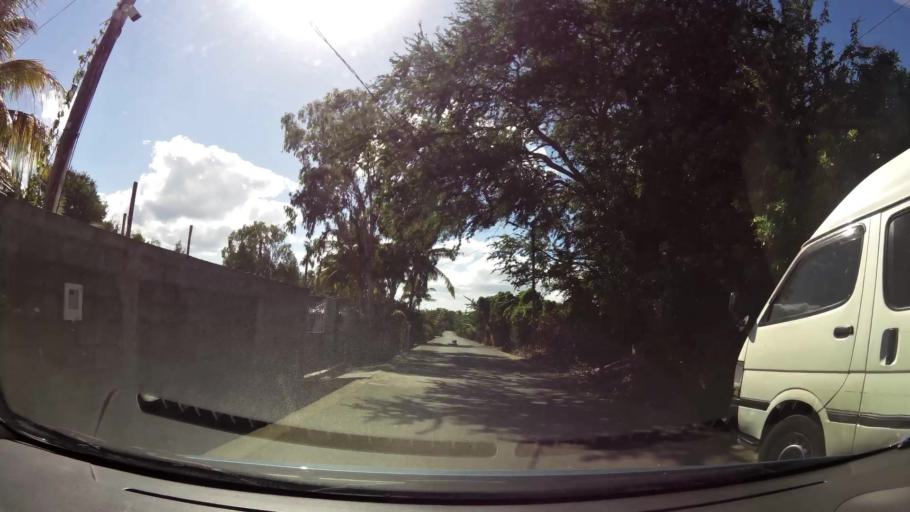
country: MU
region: Black River
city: Cascavelle
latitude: -20.2602
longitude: 57.4193
